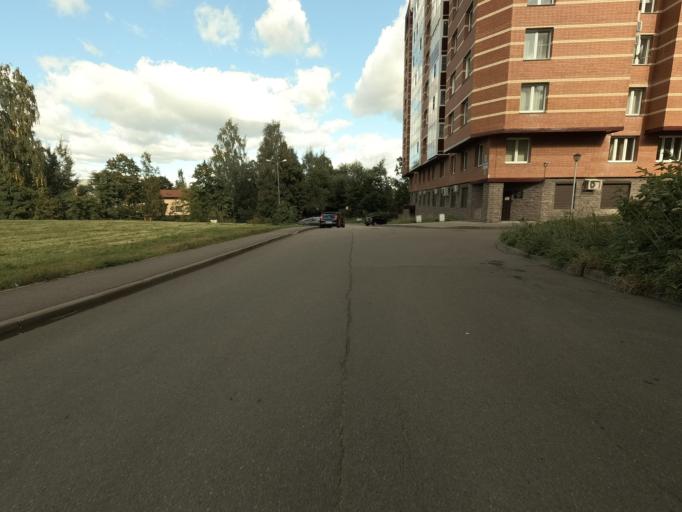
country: RU
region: St.-Petersburg
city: Krasnogvargeisky
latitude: 59.9659
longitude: 30.4934
